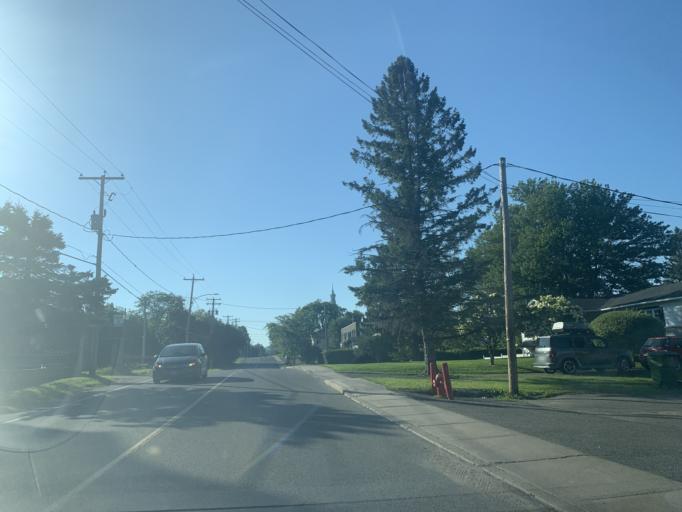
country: CA
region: Ontario
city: Hawkesbury
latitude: 45.6239
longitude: -74.6002
